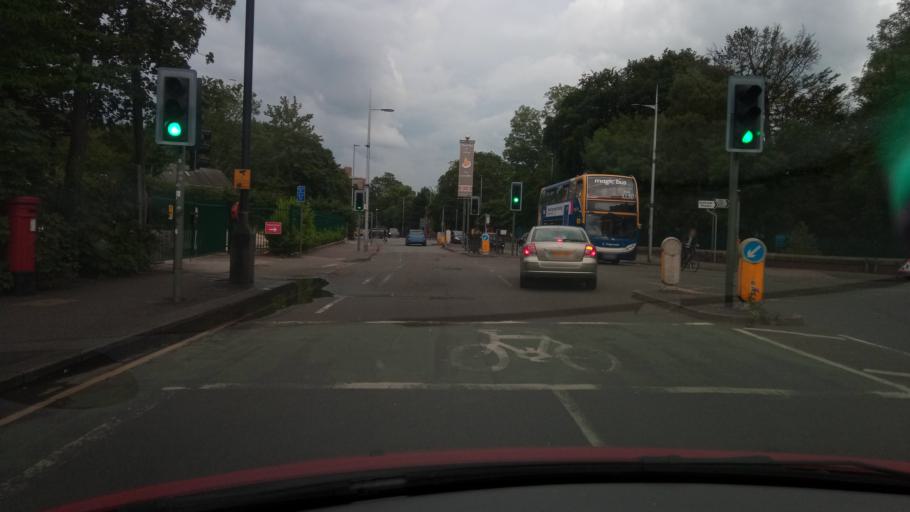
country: GB
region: England
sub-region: Manchester
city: Fallowfield
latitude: 53.4517
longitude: -2.2221
